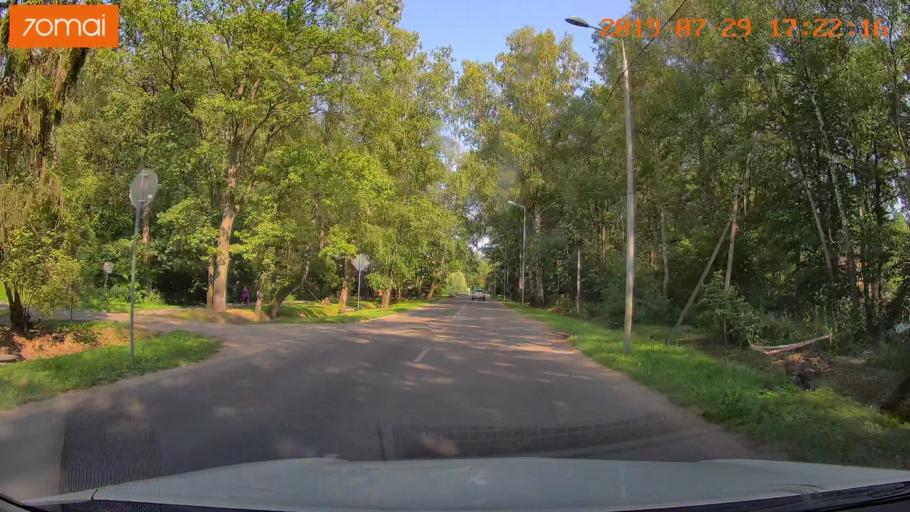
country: RU
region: Kaliningrad
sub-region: Gorod Kaliningrad
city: Kaliningrad
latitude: 54.7693
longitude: 20.4406
